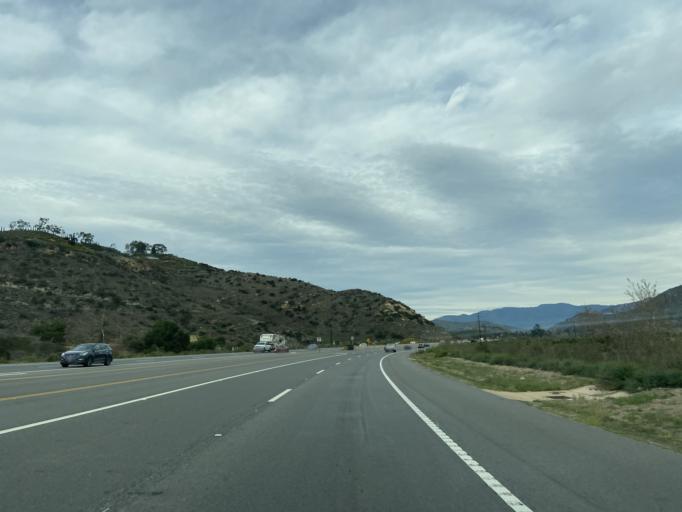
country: US
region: California
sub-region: San Diego County
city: Bonsall
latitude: 33.3196
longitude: -117.1727
